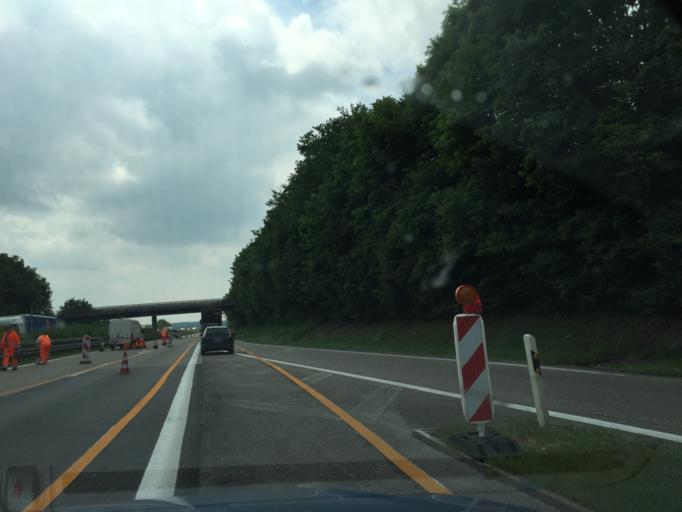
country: DE
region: Baden-Wuerttemberg
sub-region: Regierungsbezirk Stuttgart
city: Herbrechtingen
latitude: 48.5823
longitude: 10.1744
